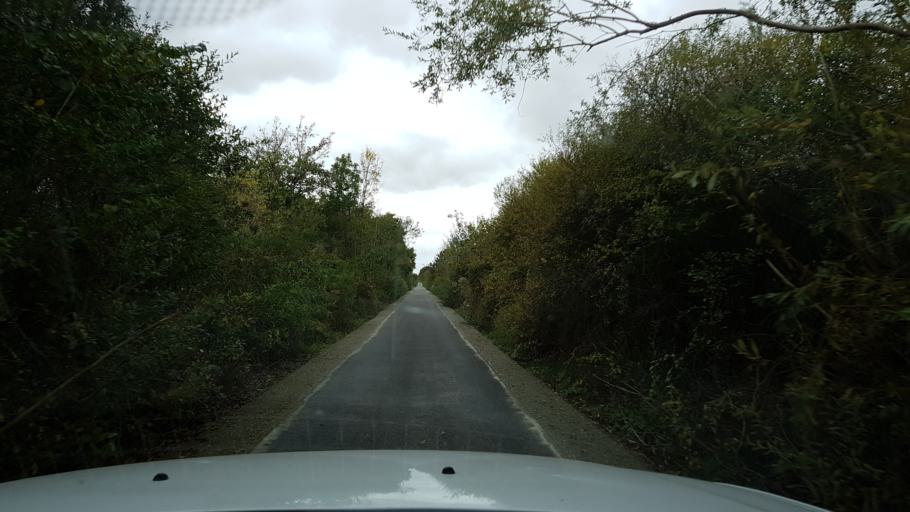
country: PL
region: West Pomeranian Voivodeship
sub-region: Powiat gryfinski
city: Moryn
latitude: 52.8667
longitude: 14.3194
